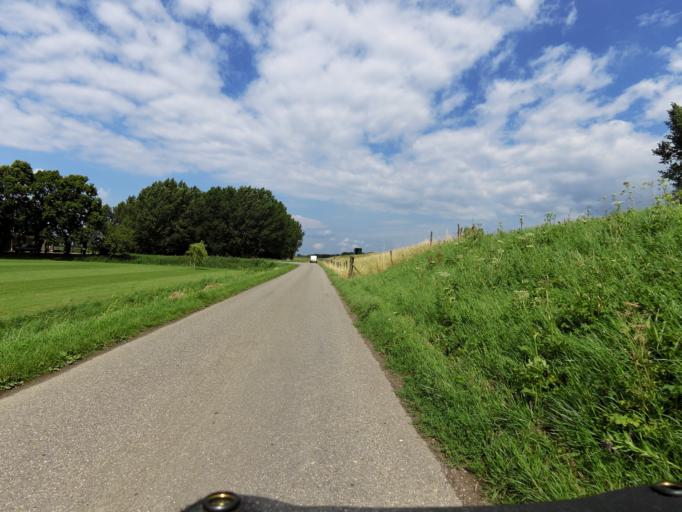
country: NL
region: South Holland
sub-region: Gemeente Strijen
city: Strijen
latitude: 51.7289
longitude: 4.6235
